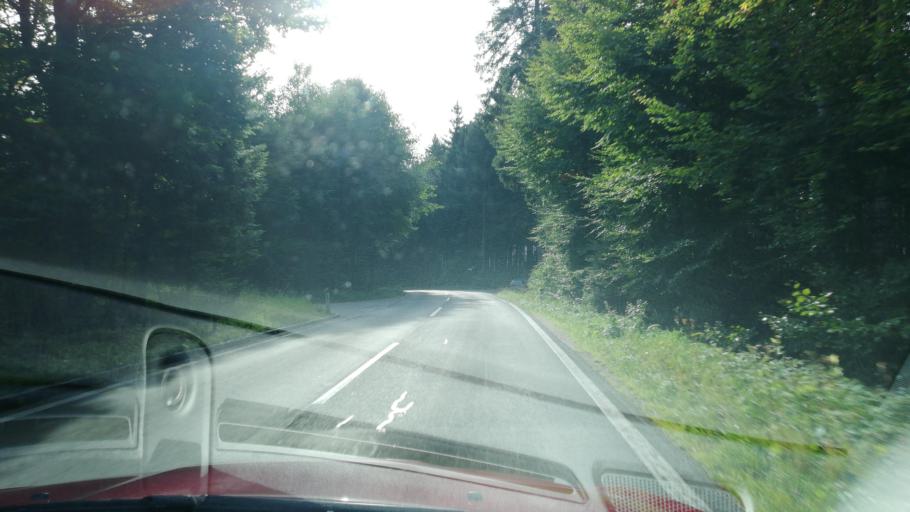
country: AT
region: Upper Austria
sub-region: Politischer Bezirk Vocklabruck
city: Redleiten
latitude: 48.1131
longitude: 13.5612
